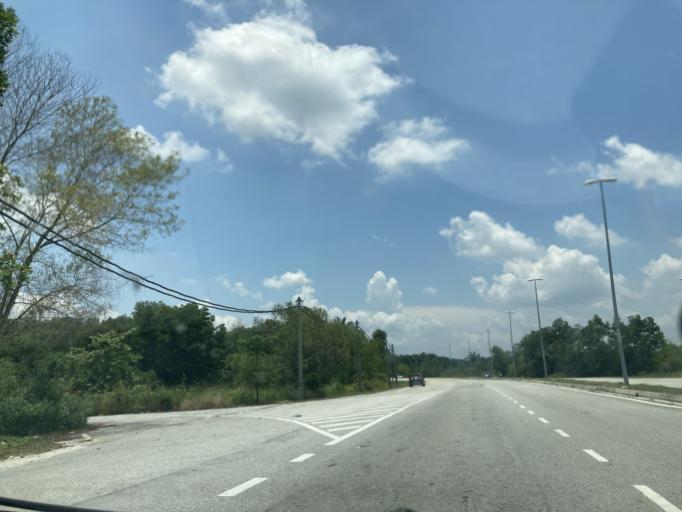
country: MY
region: Selangor
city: Ladang Seri Kundang
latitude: 3.3156
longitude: 101.5056
